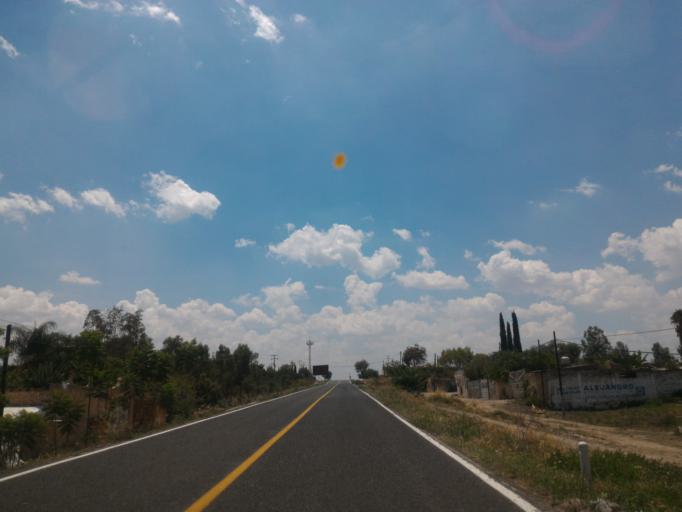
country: MX
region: Guanajuato
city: Ciudad Manuel Doblado
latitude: 20.8014
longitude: -101.9908
